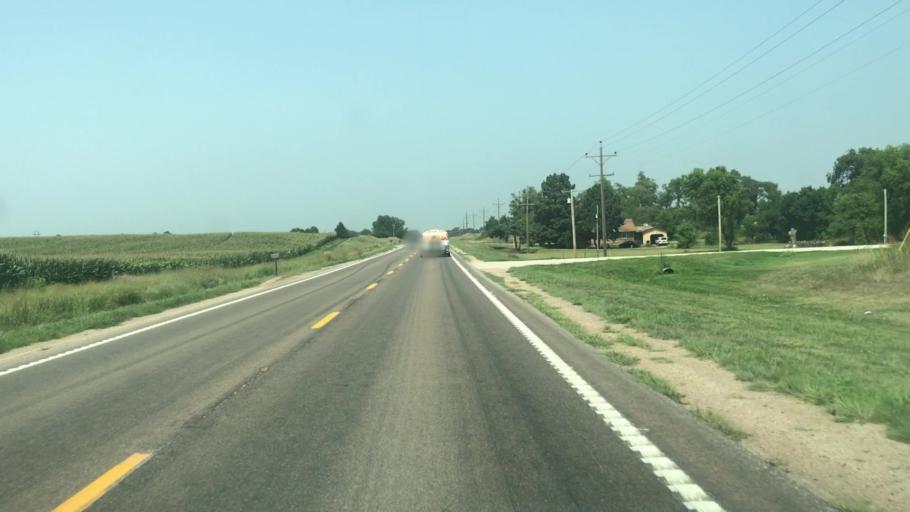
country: US
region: Nebraska
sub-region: Hall County
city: Wood River
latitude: 41.0213
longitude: -98.6075
